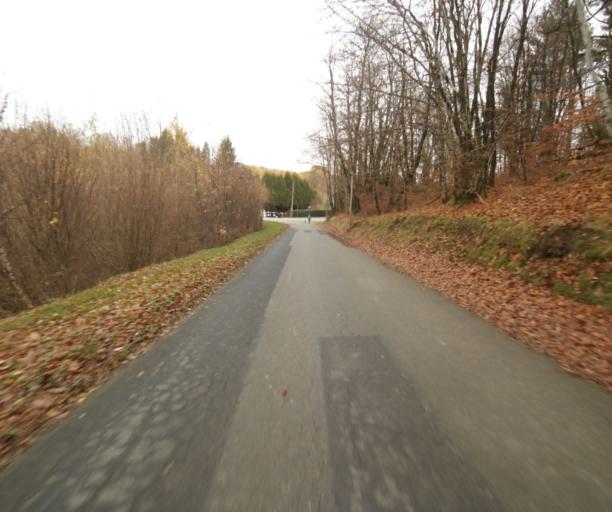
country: FR
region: Limousin
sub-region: Departement de la Correze
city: Sainte-Fortunade
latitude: 45.2178
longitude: 1.7663
